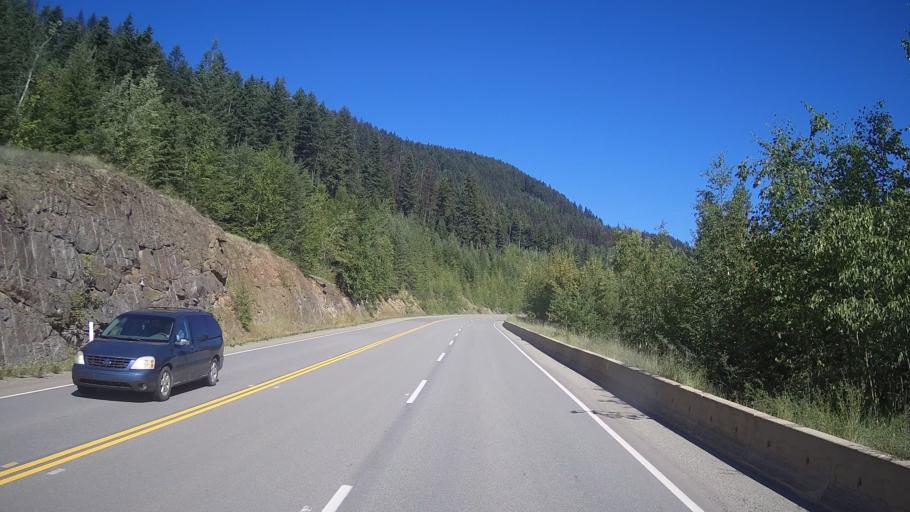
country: CA
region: British Columbia
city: Kamloops
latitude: 51.4669
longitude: -120.2508
